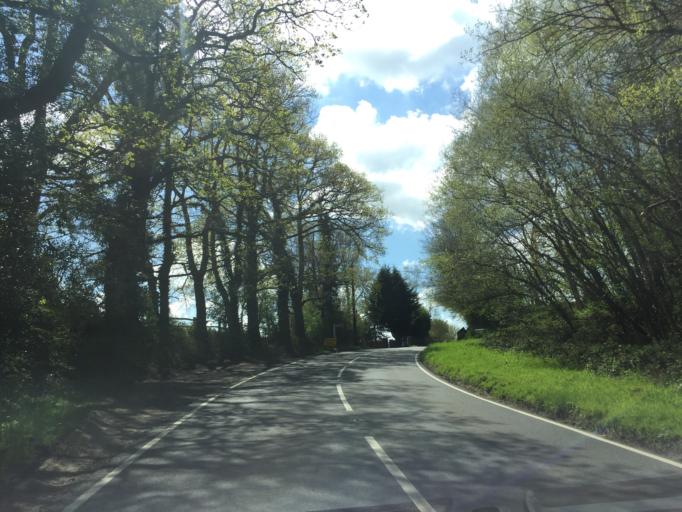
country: GB
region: England
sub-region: East Sussex
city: Crowborough
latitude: 51.1142
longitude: 0.1134
